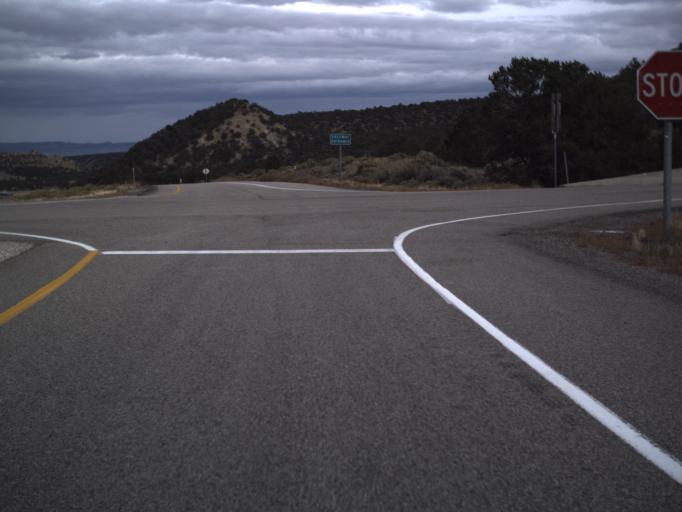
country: US
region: Utah
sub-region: Wayne County
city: Loa
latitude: 38.7564
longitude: -111.4257
